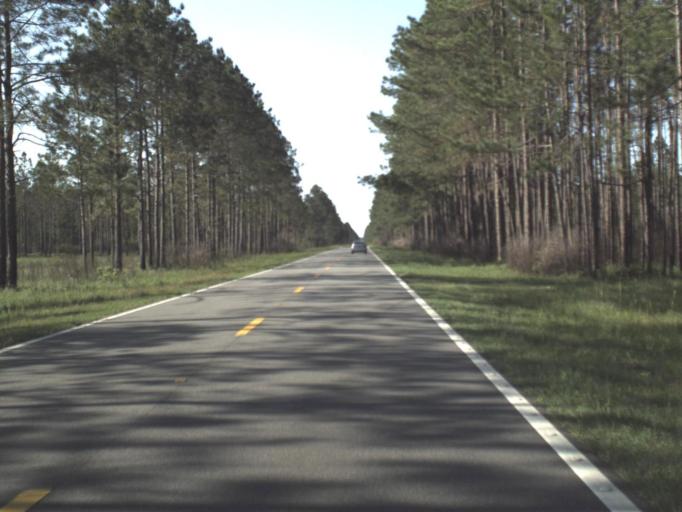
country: US
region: Florida
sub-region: Gulf County
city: Wewahitchka
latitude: 30.0420
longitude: -84.9835
